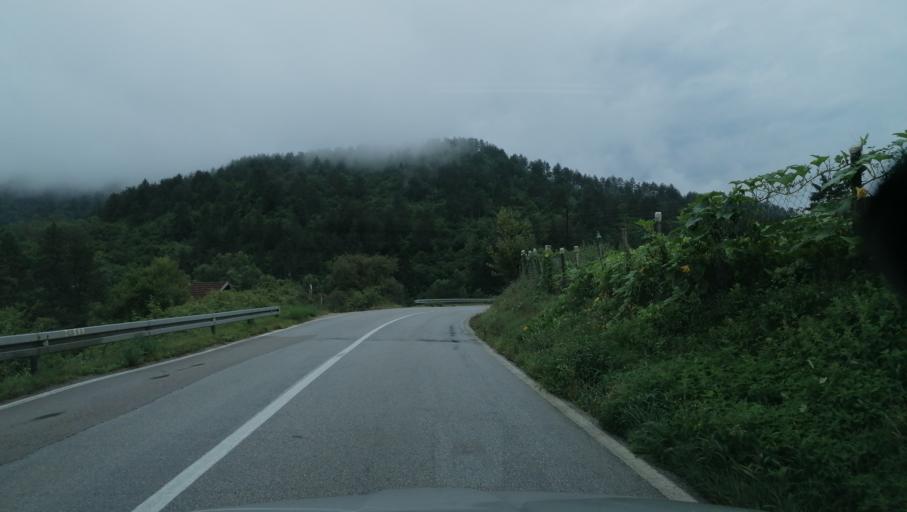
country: BA
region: Republika Srpska
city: Visegrad
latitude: 43.7850
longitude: 19.3247
